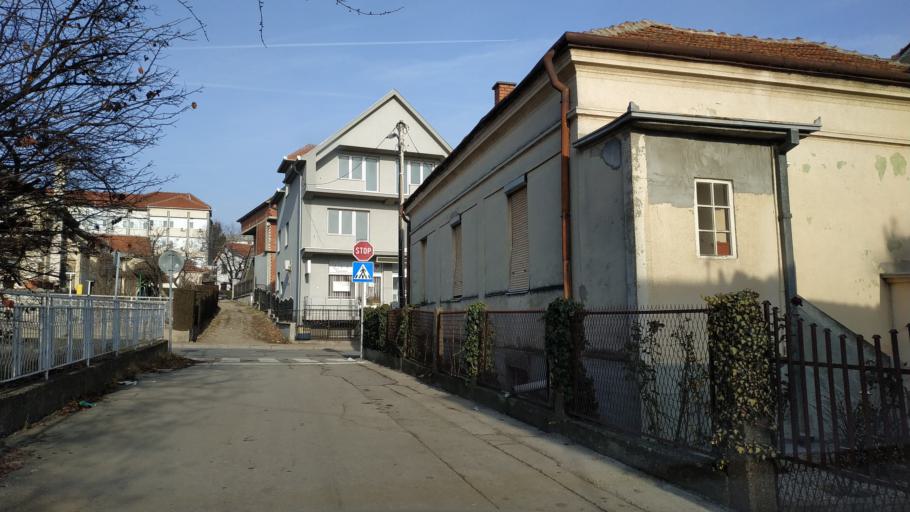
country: RS
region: Central Serbia
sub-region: Nisavski Okrug
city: Aleksinac
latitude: 43.5389
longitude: 21.7016
